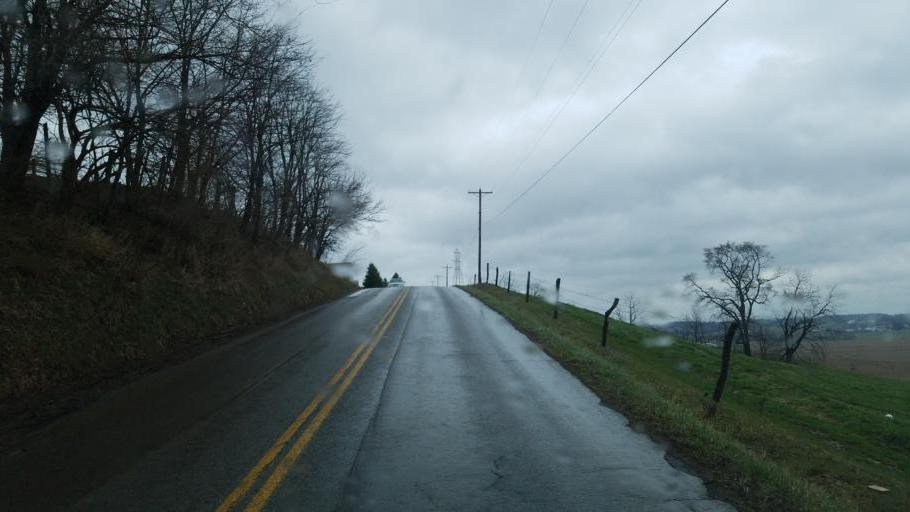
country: US
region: Ohio
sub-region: Wayne County
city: Apple Creek
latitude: 40.6298
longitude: -81.8129
